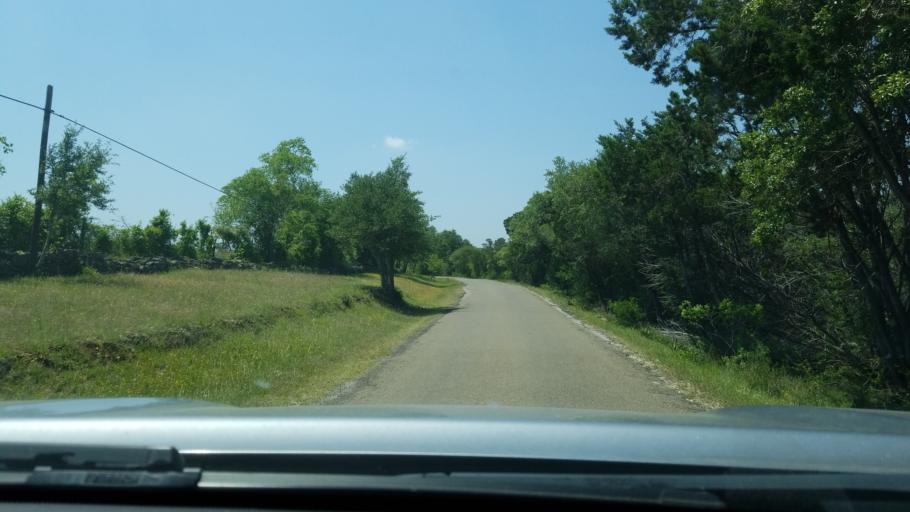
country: US
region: Texas
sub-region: Blanco County
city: Blanco
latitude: 30.0038
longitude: -98.4270
